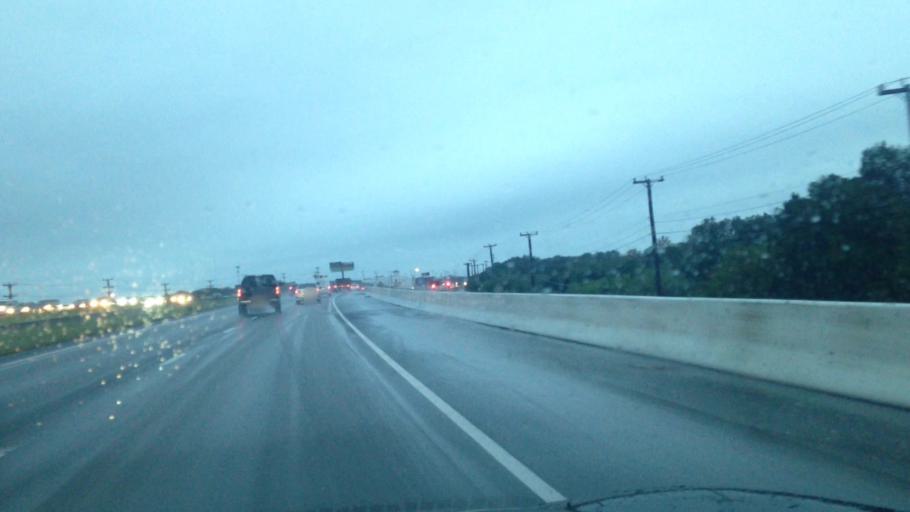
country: US
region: Texas
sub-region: Bexar County
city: Shavano Park
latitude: 29.5936
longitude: -98.5757
